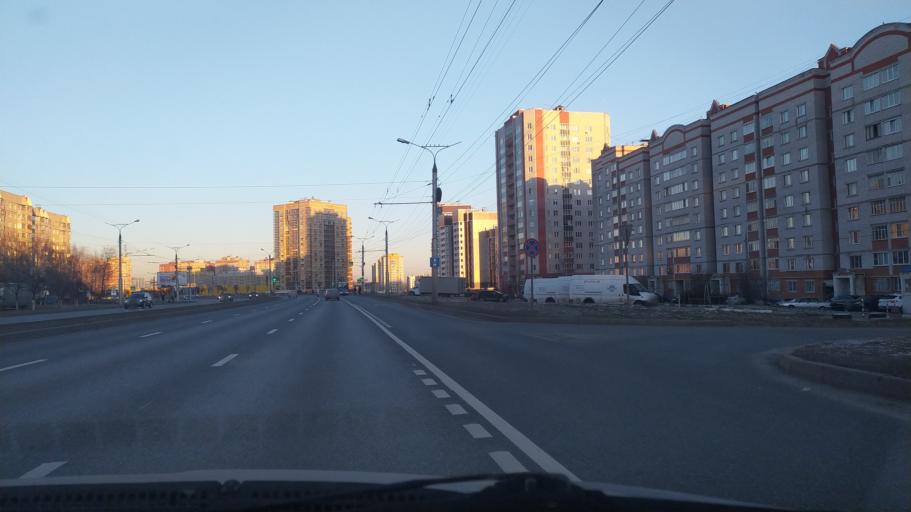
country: RU
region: Chuvashia
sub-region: Cheboksarskiy Rayon
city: Cheboksary
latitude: 56.1059
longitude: 47.3224
